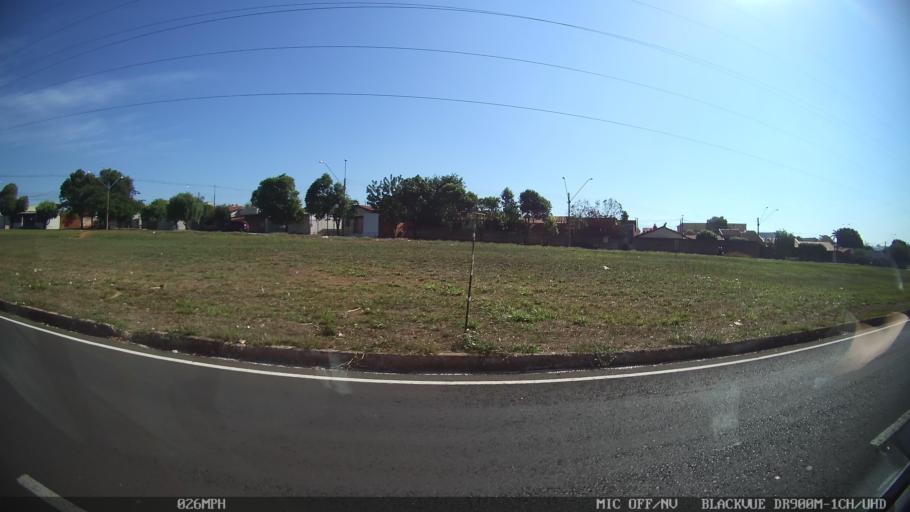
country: BR
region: Sao Paulo
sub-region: Sao Jose Do Rio Preto
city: Sao Jose do Rio Preto
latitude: -20.7649
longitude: -49.3797
